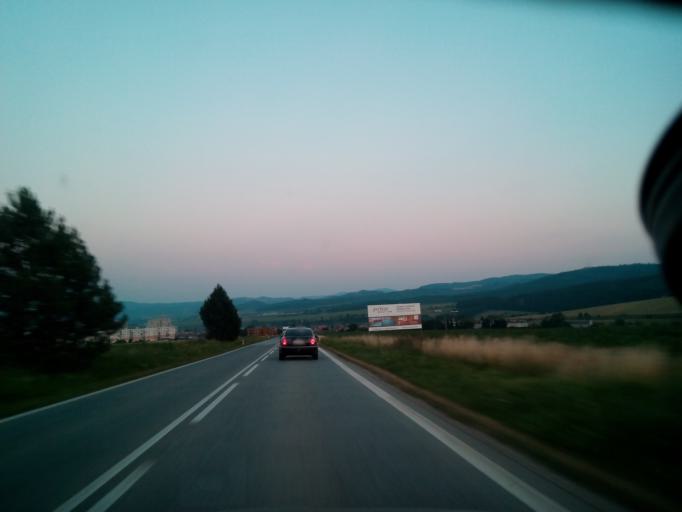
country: SK
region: Kosicky
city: Spisska Nova Ves
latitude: 48.9632
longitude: 20.5034
